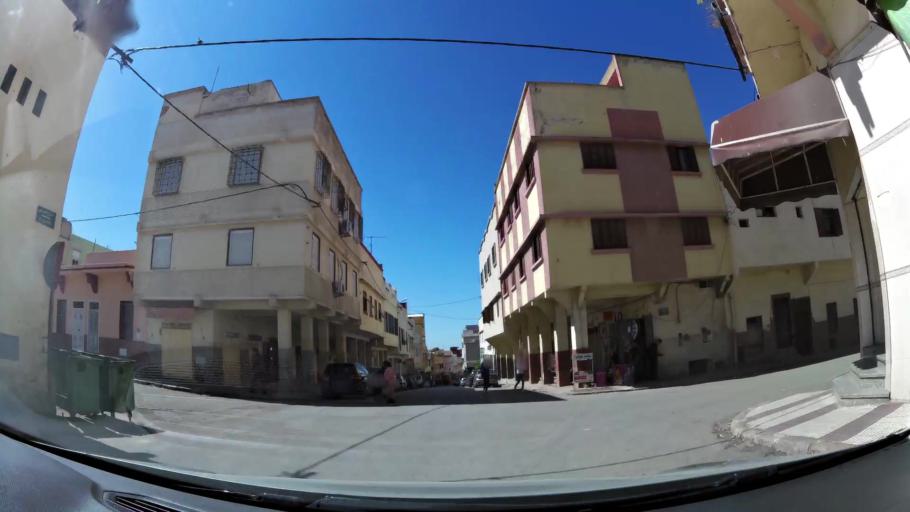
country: MA
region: Meknes-Tafilalet
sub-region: Meknes
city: Meknes
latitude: 33.8886
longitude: -5.5708
